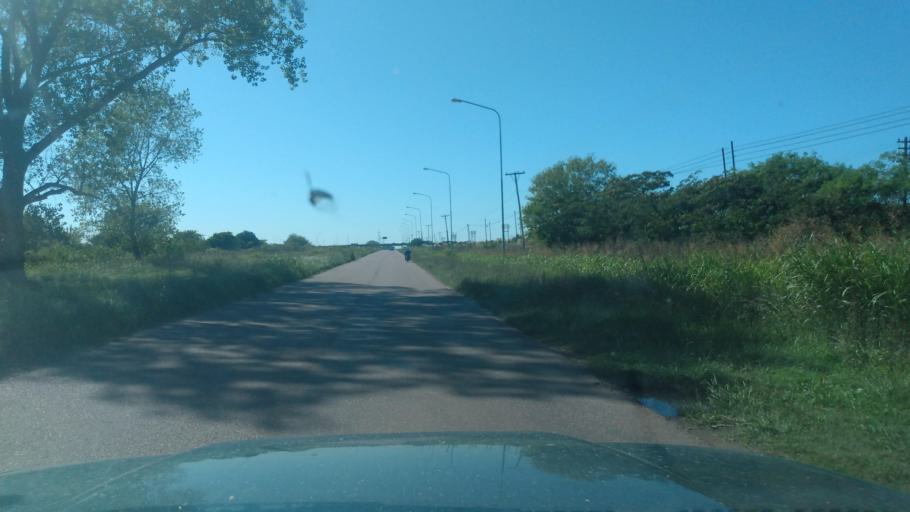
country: AR
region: Buenos Aires
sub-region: Partido de Lujan
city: Lujan
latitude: -34.5868
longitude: -59.0459
